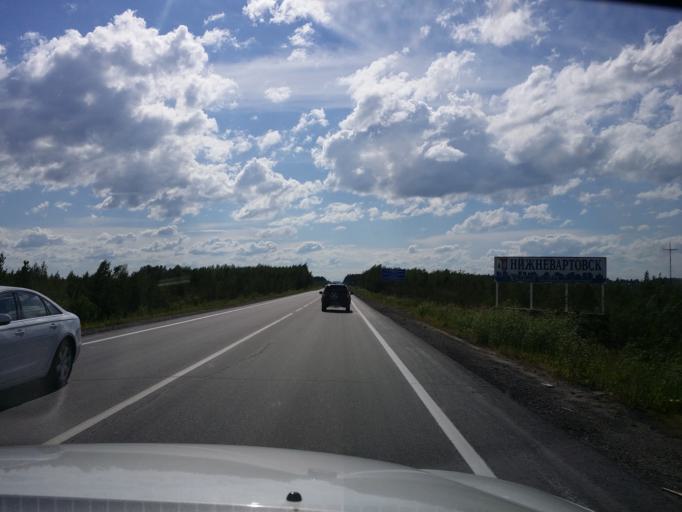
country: RU
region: Khanty-Mansiyskiy Avtonomnyy Okrug
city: Nizhnevartovsk
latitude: 60.9560
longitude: 76.7164
